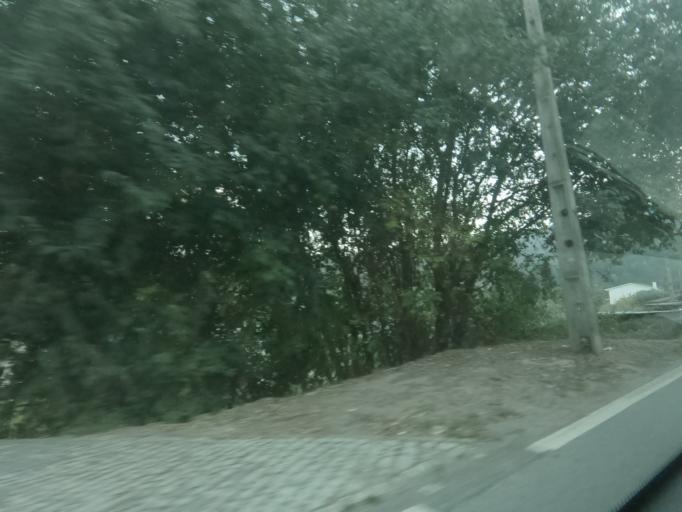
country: PT
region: Vila Real
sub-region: Peso da Regua
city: Godim
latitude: 41.1507
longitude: -7.8105
